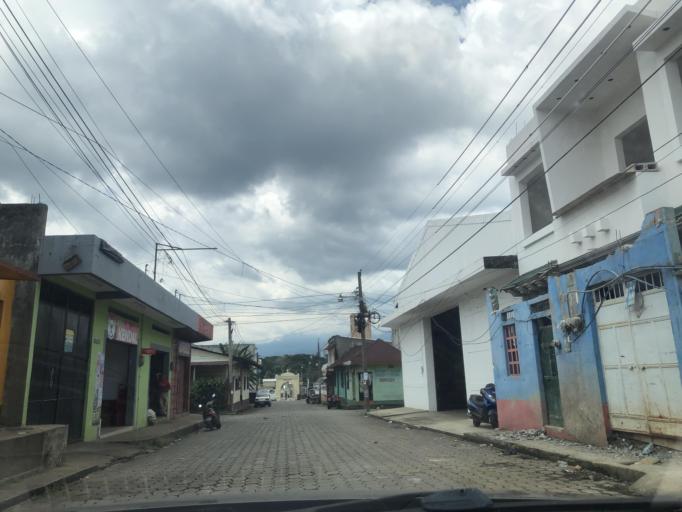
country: GT
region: Quetzaltenango
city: Coatepeque
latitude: 14.7086
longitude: -91.8649
